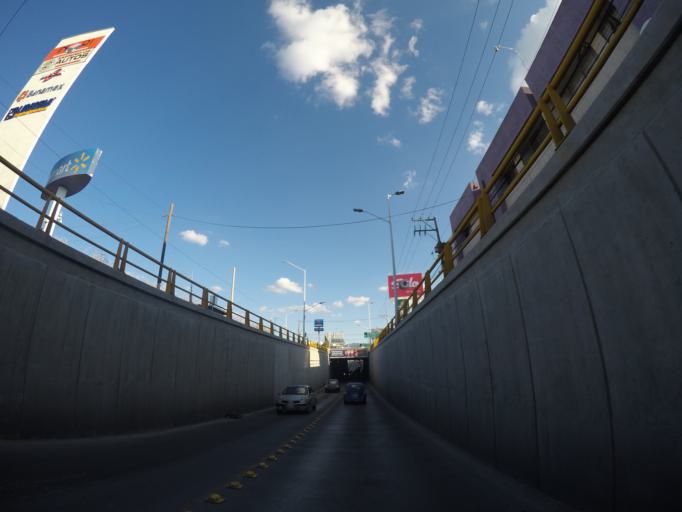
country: MX
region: San Luis Potosi
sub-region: San Luis Potosi
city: San Luis Potosi
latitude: 22.1662
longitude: -101.0013
